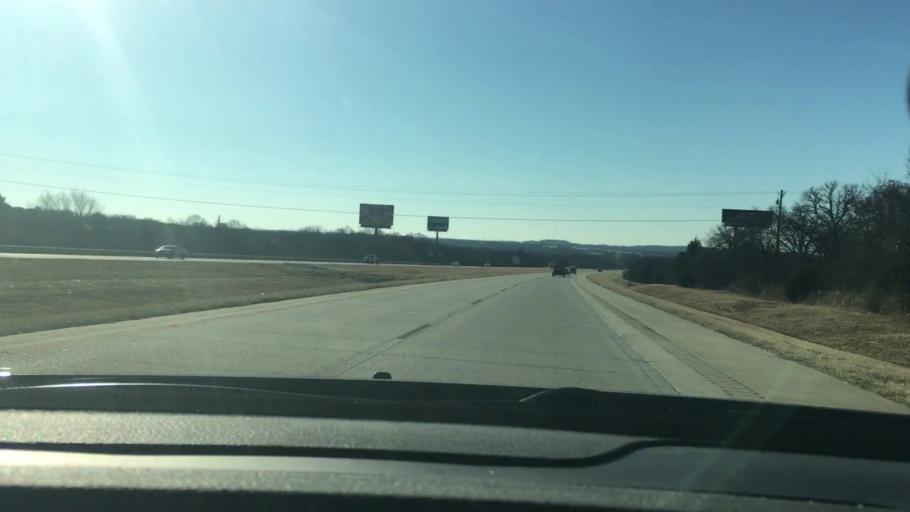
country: US
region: Oklahoma
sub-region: Carter County
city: Ardmore
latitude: 34.0577
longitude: -97.1491
